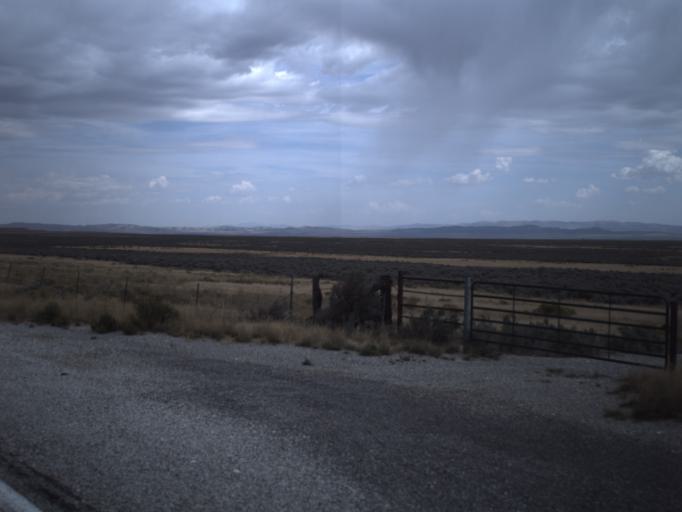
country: US
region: Idaho
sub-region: Oneida County
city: Malad City
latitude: 41.9284
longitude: -113.0909
